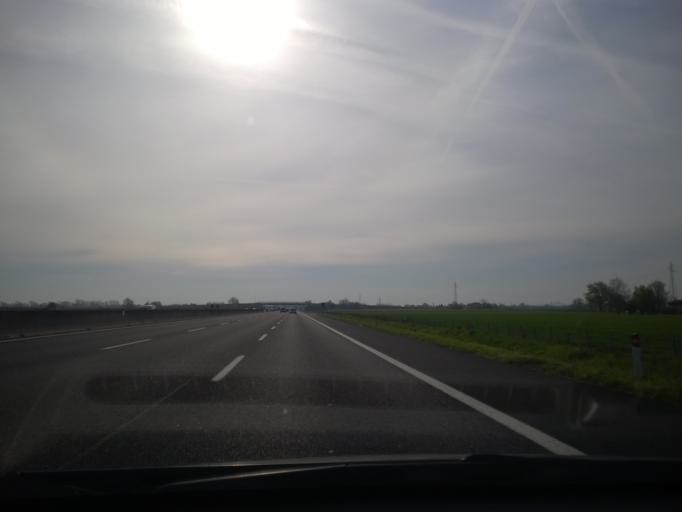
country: IT
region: Emilia-Romagna
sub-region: Provincia di Ravenna
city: Granarolo
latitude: 44.2944
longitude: 11.9782
